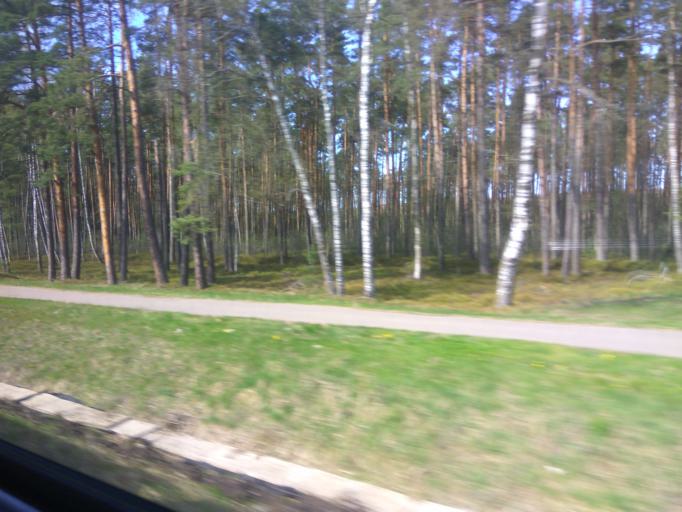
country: LV
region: Babite
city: Pinki
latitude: 56.9658
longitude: 23.9121
